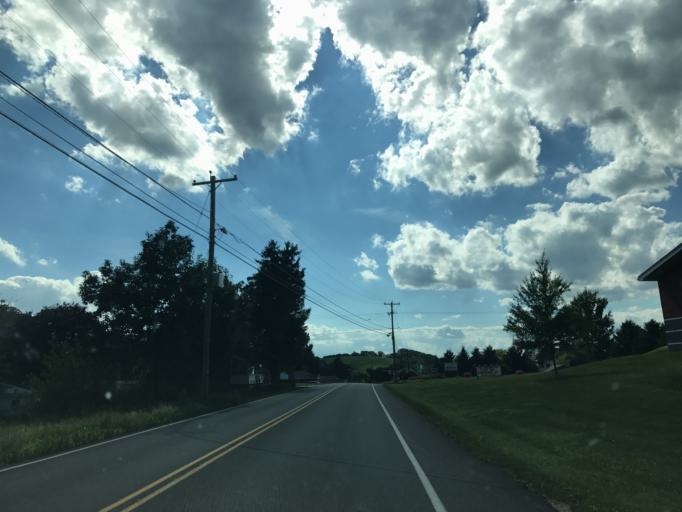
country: US
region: Maryland
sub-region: Carroll County
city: Manchester
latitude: 39.7631
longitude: -76.8551
